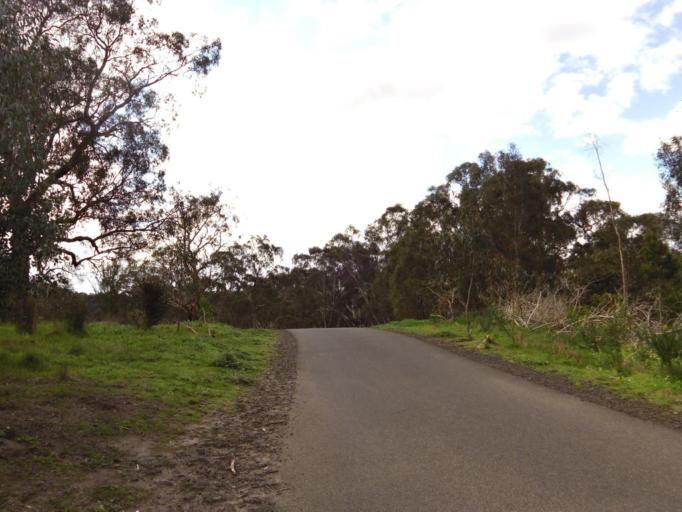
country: AU
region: Victoria
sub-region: Banyule
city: Darch
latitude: -37.7506
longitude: 145.1212
